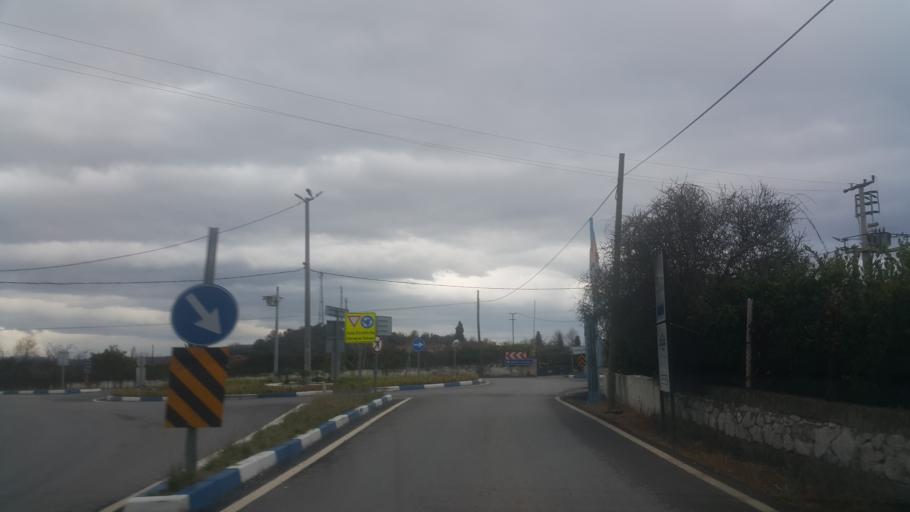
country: TR
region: Izmir
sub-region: Seferihisar
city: Seferhisar
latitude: 38.1886
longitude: 26.8078
